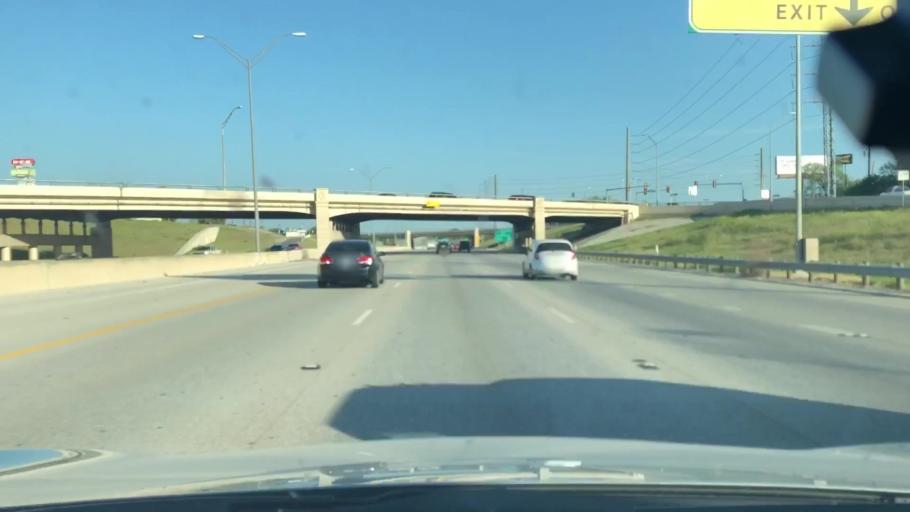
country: US
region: Texas
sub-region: Bexar County
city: San Antonio
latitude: 29.3758
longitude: -98.4660
